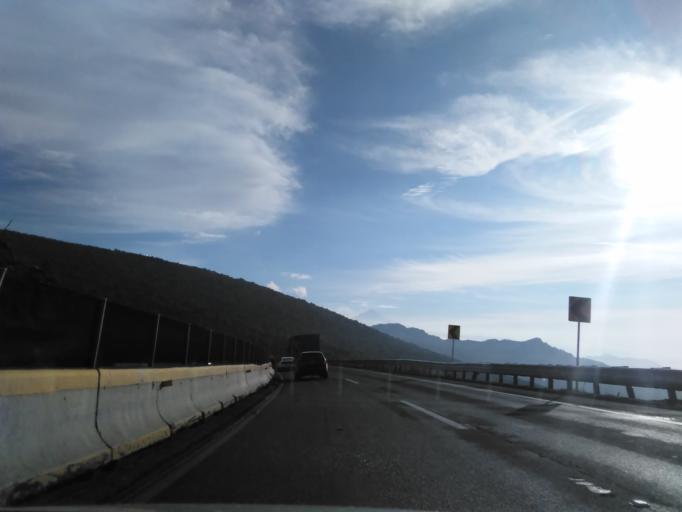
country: MX
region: Morelos
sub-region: Tepoztlan
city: Santa Catarina
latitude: 19.0197
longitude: -99.1461
